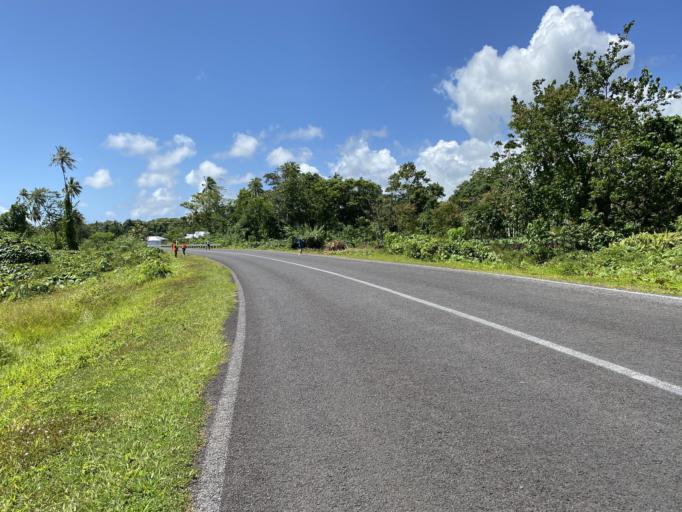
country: WS
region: Gagaifomauga
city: Safotu
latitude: -13.5086
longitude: -172.3014
